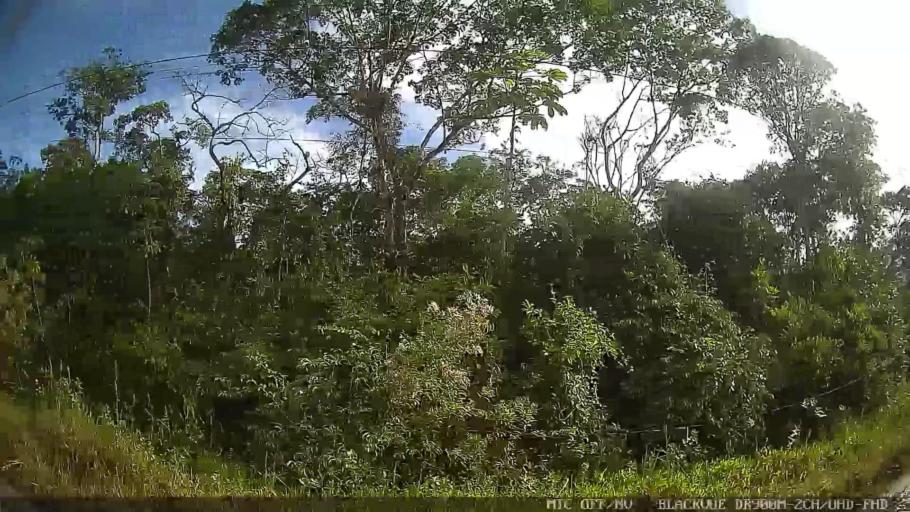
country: BR
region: Sao Paulo
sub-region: Itanhaem
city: Itanhaem
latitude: -24.1999
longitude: -46.8922
